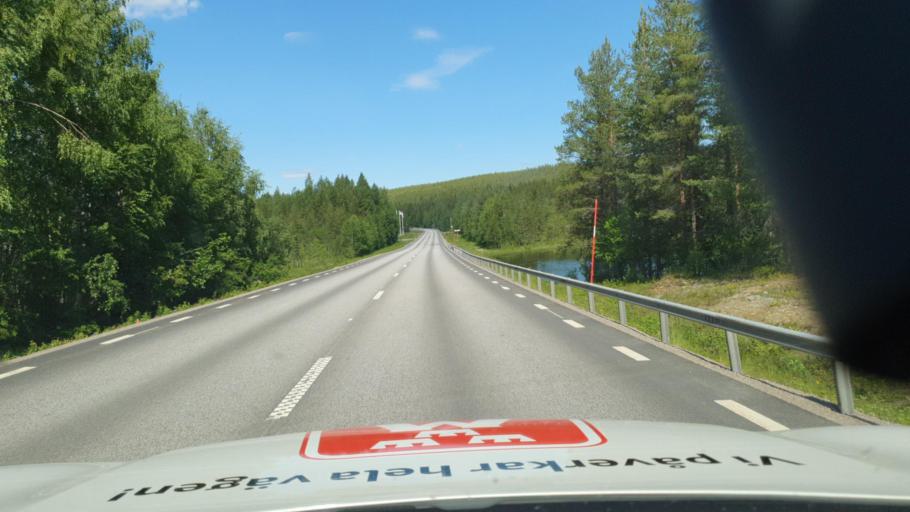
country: SE
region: Vaesterbotten
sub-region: Skelleftea Kommun
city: Boliden
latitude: 64.8927
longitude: 20.3754
